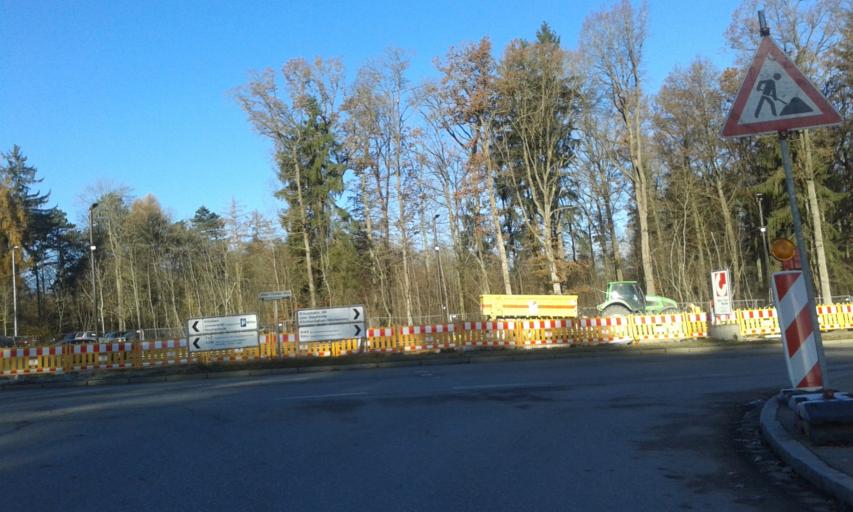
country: DE
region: Baden-Wuerttemberg
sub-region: Tuebingen Region
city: Dornstadt
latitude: 48.4256
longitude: 9.9560
